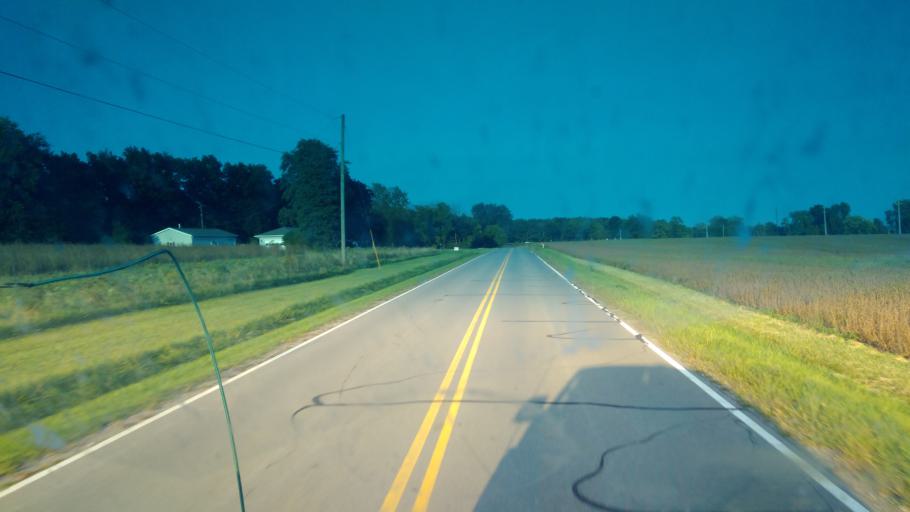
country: US
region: Ohio
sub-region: Crawford County
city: Bucyrus
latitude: 40.8356
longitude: -82.8621
